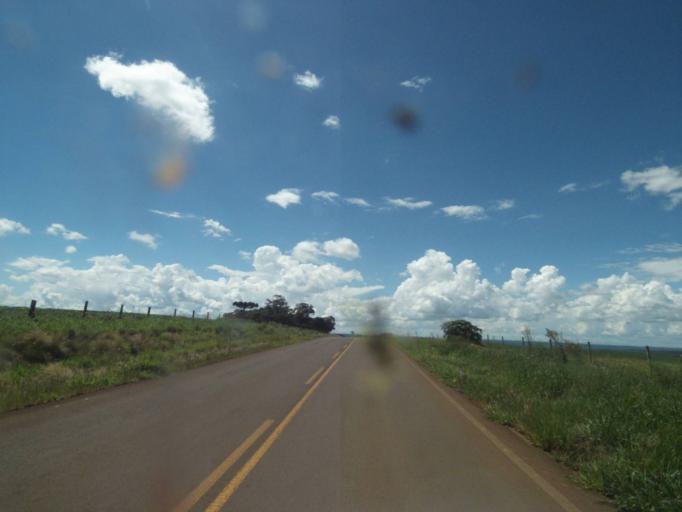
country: BR
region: Parana
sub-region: Pinhao
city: Pinhao
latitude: -25.8053
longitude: -52.0725
